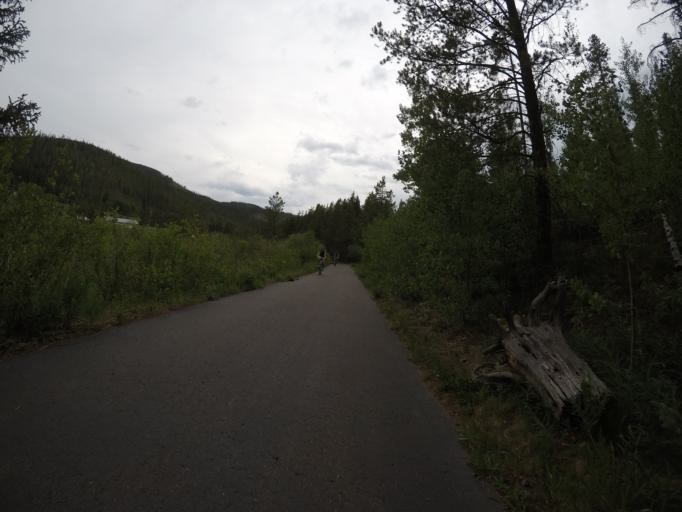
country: US
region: Colorado
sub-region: Grand County
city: Fraser
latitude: 39.8962
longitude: -105.7674
